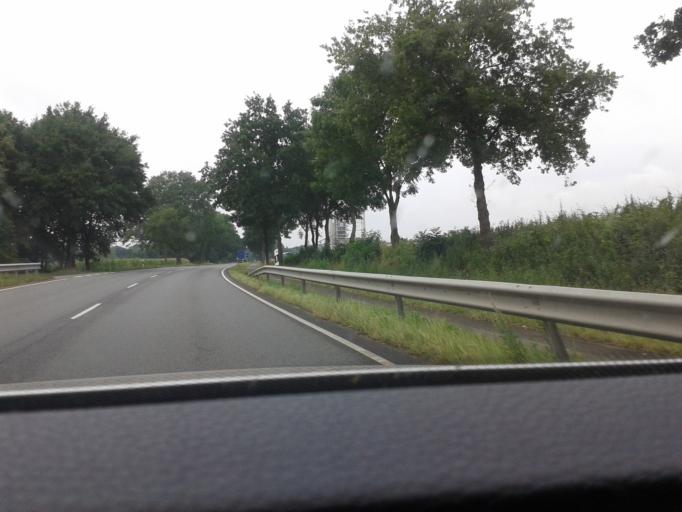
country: DE
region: Lower Saxony
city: Osloss
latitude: 52.4741
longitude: 10.6633
